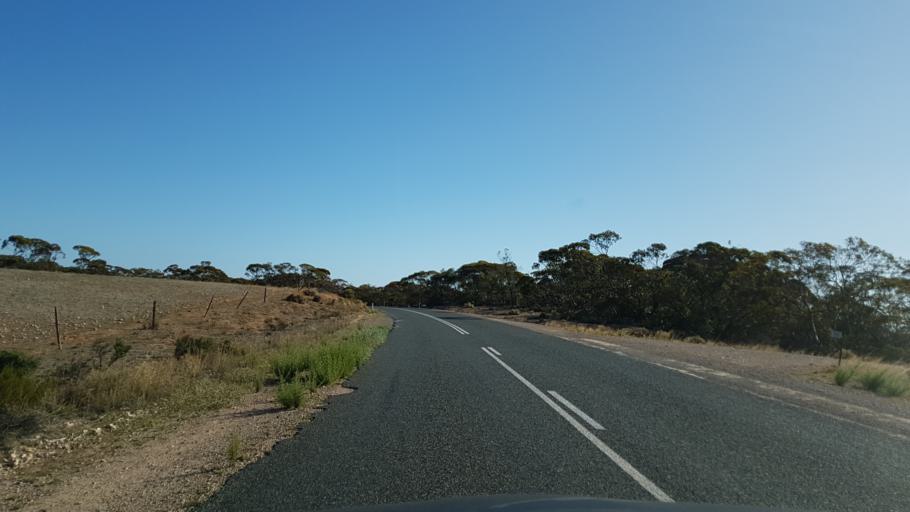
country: AU
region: South Australia
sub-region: Mid Murray
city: Mannum
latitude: -34.7959
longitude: 139.5034
